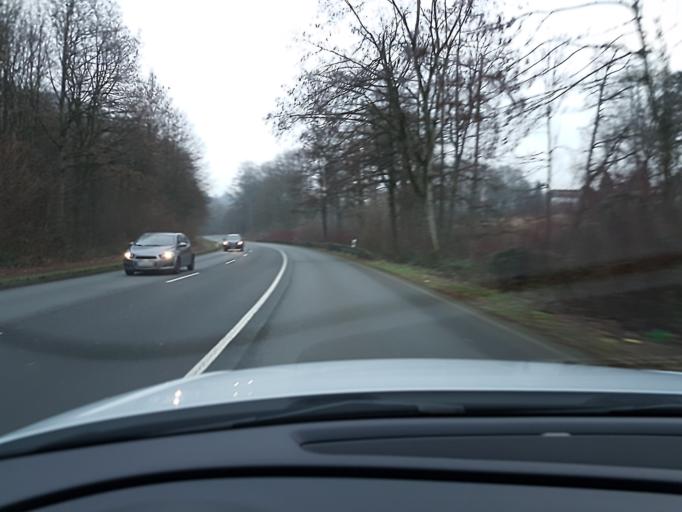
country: DE
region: North Rhine-Westphalia
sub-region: Regierungsbezirk Dusseldorf
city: Muelheim (Ruhr)
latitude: 51.4205
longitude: 6.9021
